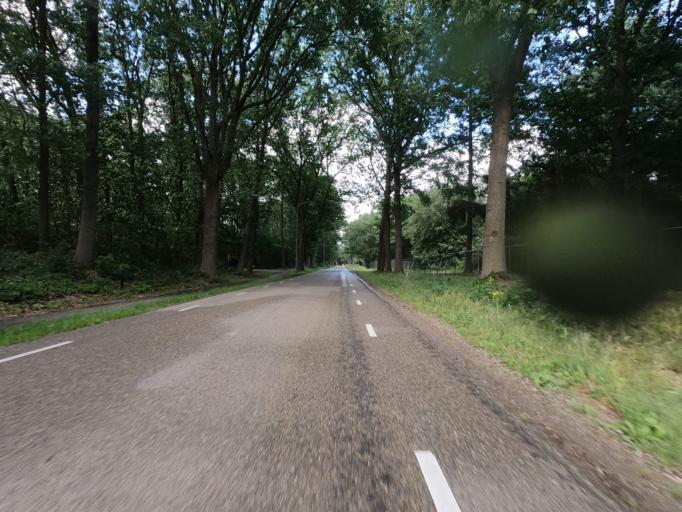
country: NL
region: North Brabant
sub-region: Gemeente Landerd
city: Reek
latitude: 51.7320
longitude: 5.6820
